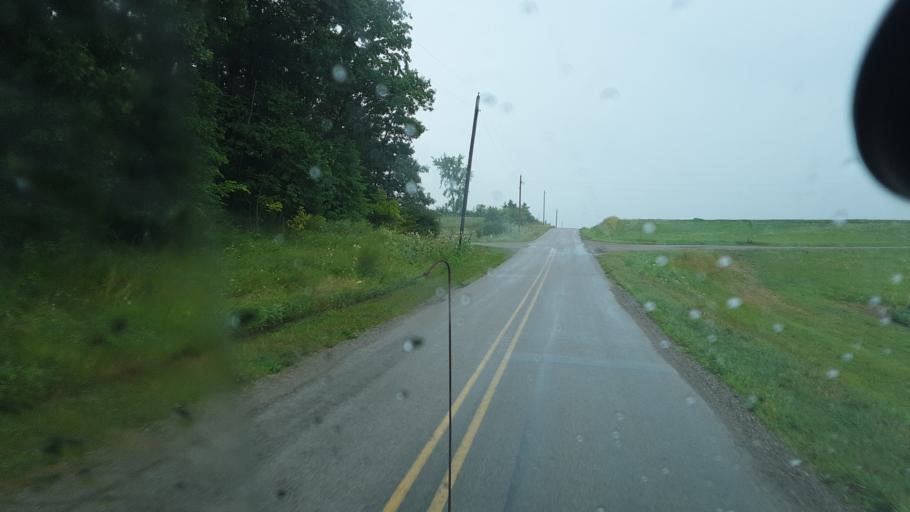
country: US
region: Indiana
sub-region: DeKalb County
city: Butler
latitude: 41.4636
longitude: -84.8141
